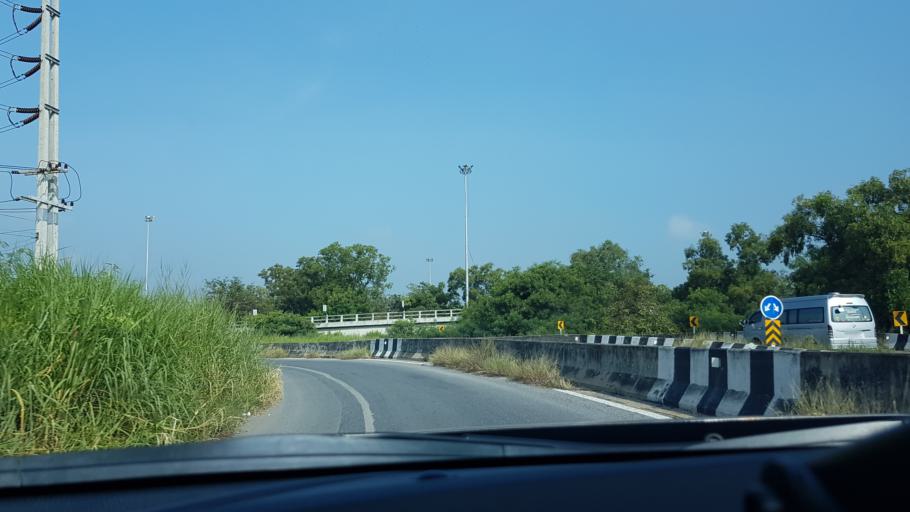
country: TH
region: Phra Nakhon Si Ayutthaya
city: Bang Pa-in
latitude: 14.1541
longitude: 100.5682
